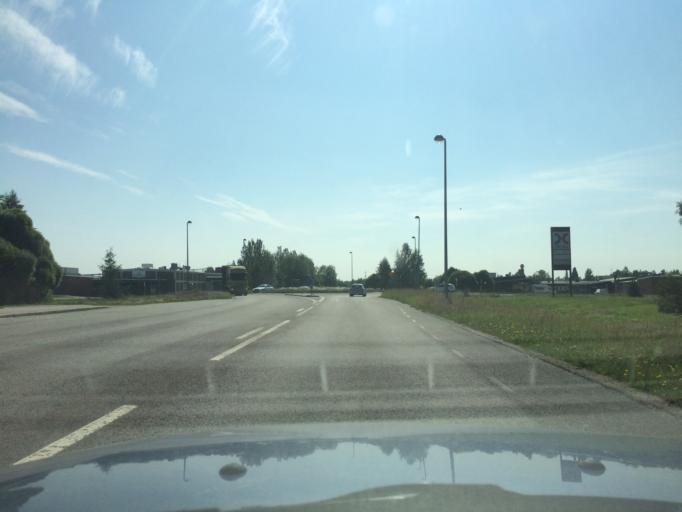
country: SE
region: Norrbotten
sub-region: Pitea Kommun
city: Bergsviken
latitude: 65.3468
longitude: 21.4050
